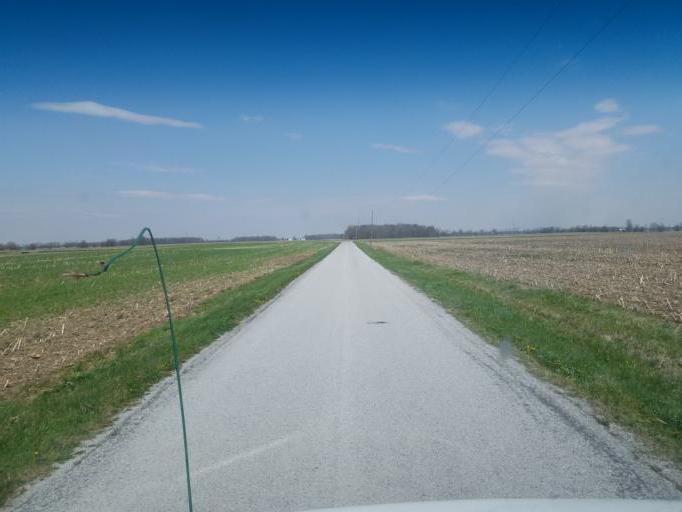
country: US
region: Ohio
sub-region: Hardin County
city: Kenton
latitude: 40.6993
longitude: -83.5473
